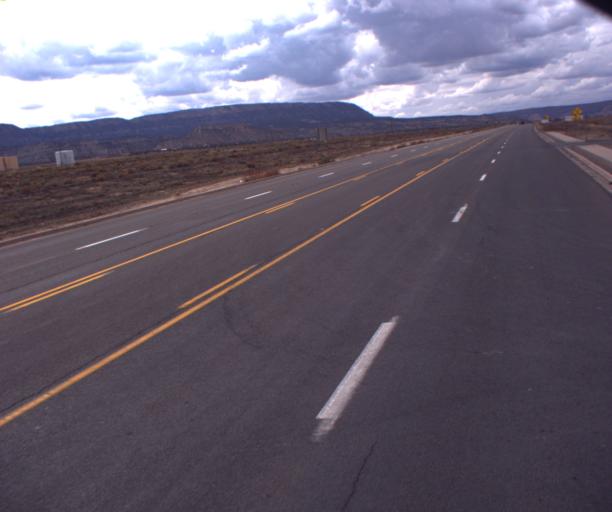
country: US
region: Arizona
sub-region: Navajo County
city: Kayenta
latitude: 36.7070
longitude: -110.2525
